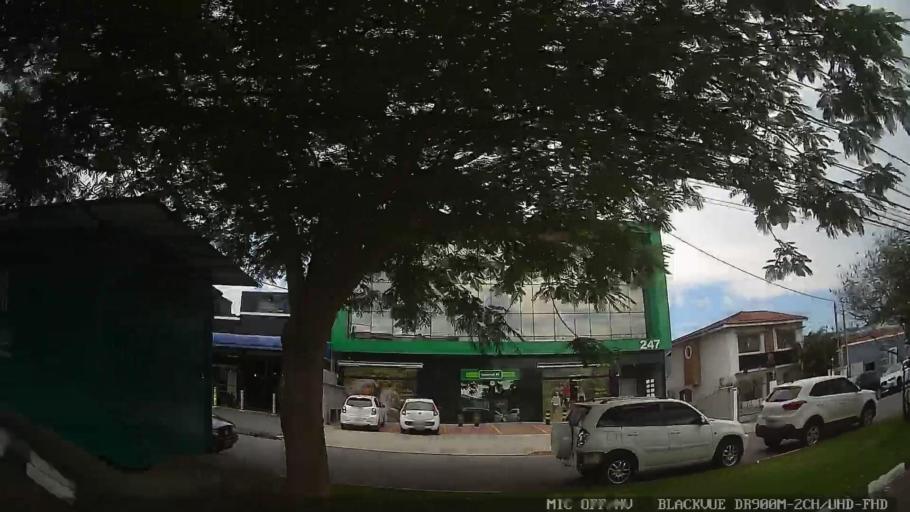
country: BR
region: Sao Paulo
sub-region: Atibaia
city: Atibaia
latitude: -23.1482
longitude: -46.5548
